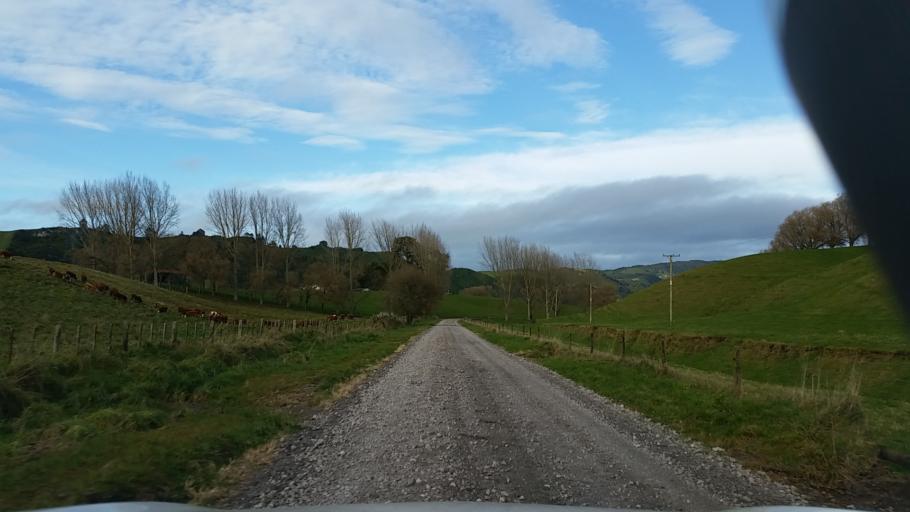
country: NZ
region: Bay of Plenty
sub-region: Rotorua District
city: Rotorua
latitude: -38.3140
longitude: 176.3021
